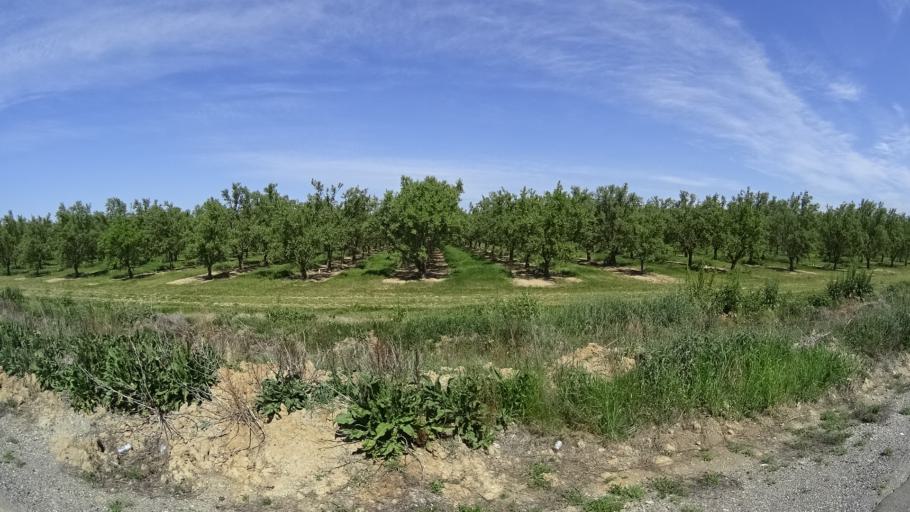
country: US
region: California
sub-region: Glenn County
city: Orland
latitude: 39.6533
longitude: -122.1908
